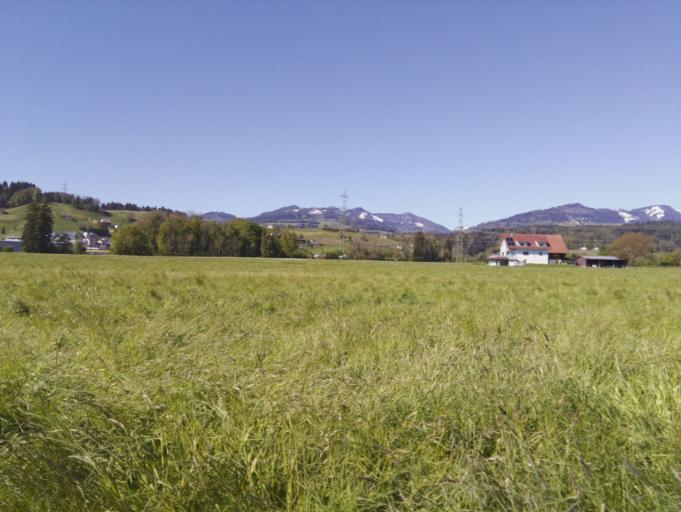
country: CH
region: Saint Gallen
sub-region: Wahlkreis See-Gaster
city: Schmerikon
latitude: 47.2200
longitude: 8.9592
